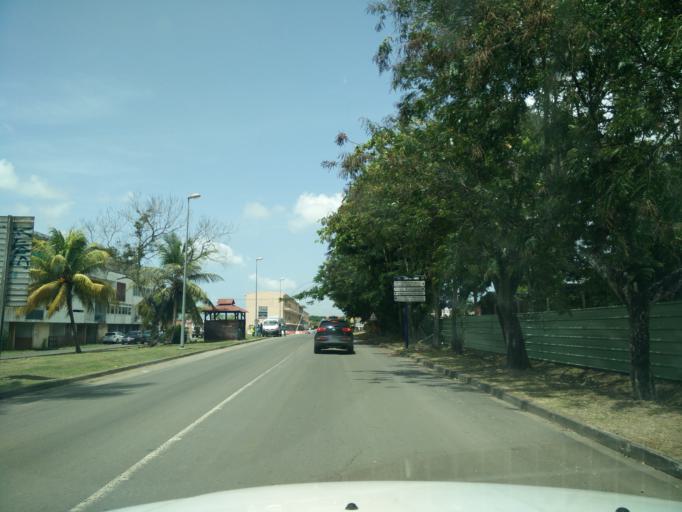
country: GP
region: Guadeloupe
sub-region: Guadeloupe
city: Pointe-a-Pitre
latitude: 16.2593
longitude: -61.5254
